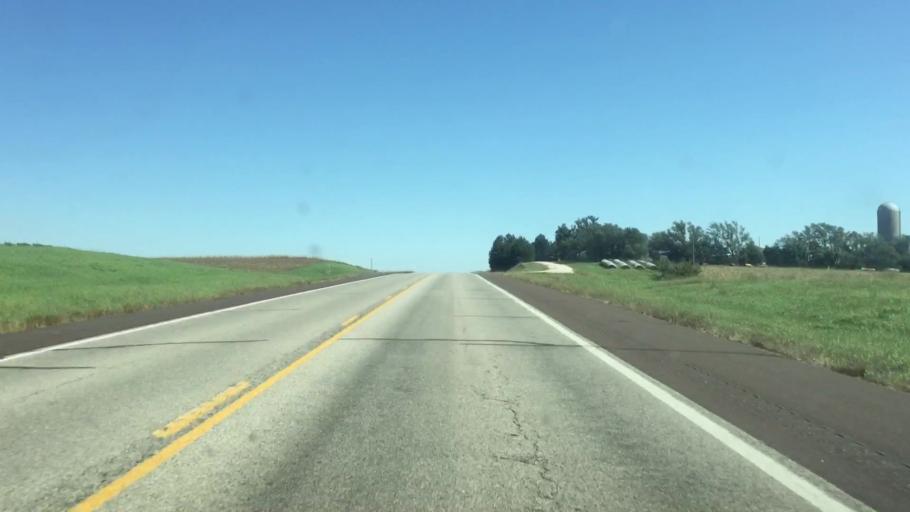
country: US
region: Kansas
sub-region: Nemaha County
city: Seneca
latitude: 39.8421
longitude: -96.3003
